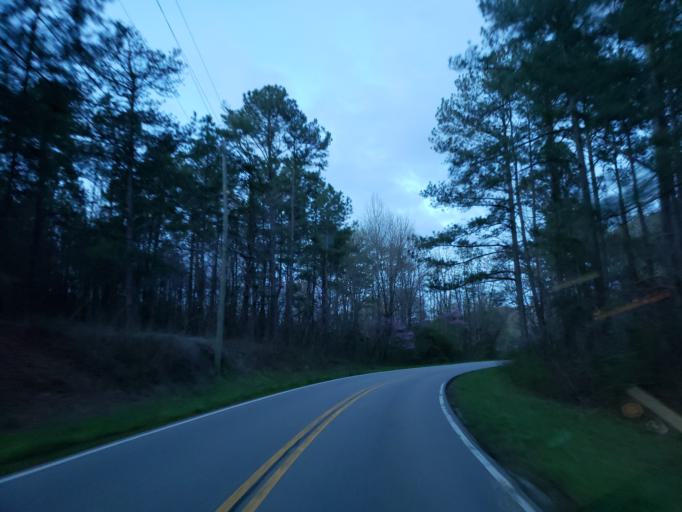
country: US
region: Georgia
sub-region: Paulding County
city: Dallas
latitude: 34.0152
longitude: -84.8735
